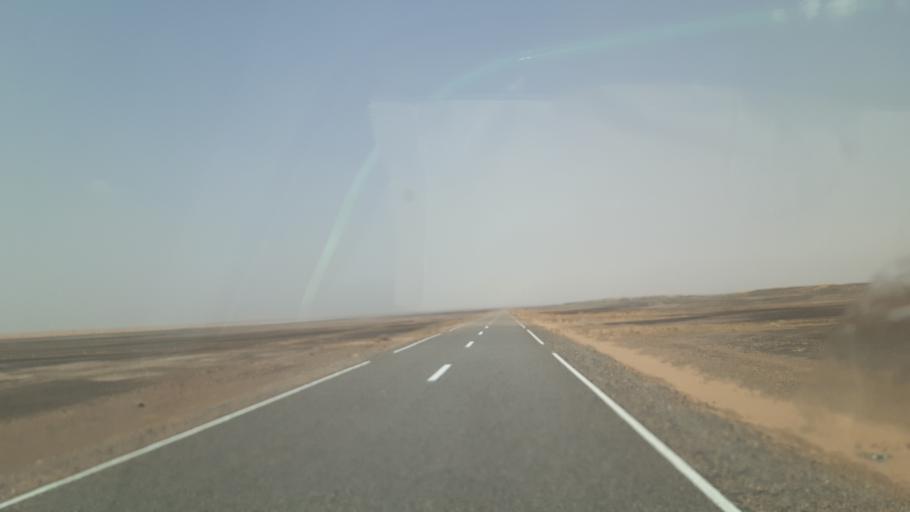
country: MA
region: Meknes-Tafilalet
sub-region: Errachidia
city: Jorf
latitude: 31.2032
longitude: -4.1049
